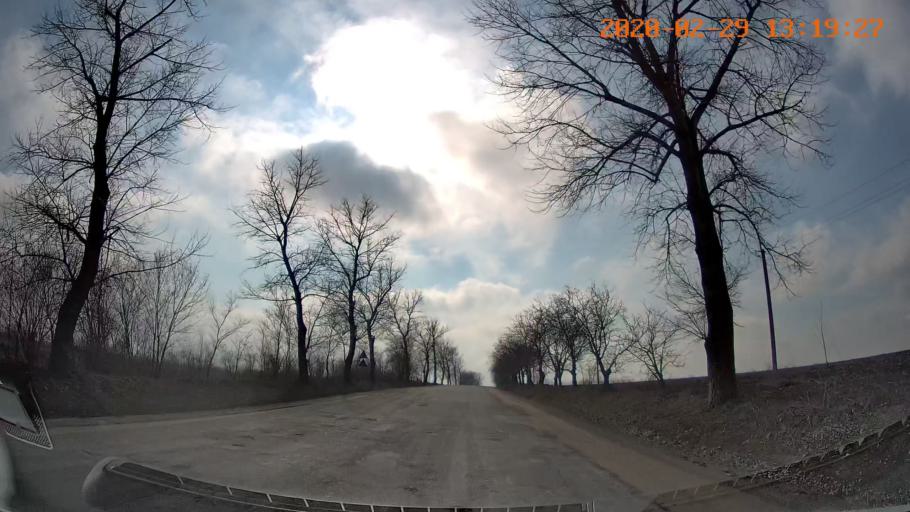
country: MD
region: Telenesti
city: Camenca
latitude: 47.9885
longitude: 28.6508
